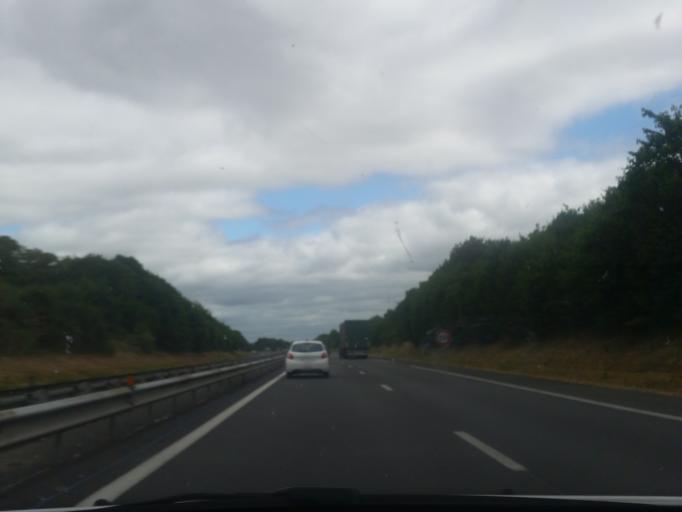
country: FR
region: Pays de la Loire
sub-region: Departement de Maine-et-Loire
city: Durtal
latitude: 47.6716
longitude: -0.2599
